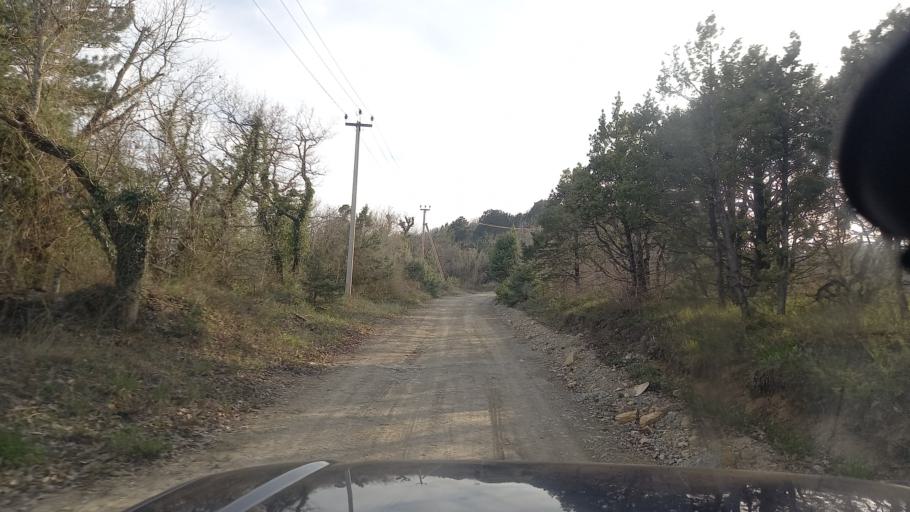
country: RU
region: Krasnodarskiy
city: Arkhipo-Osipovka
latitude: 44.3657
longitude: 38.5778
